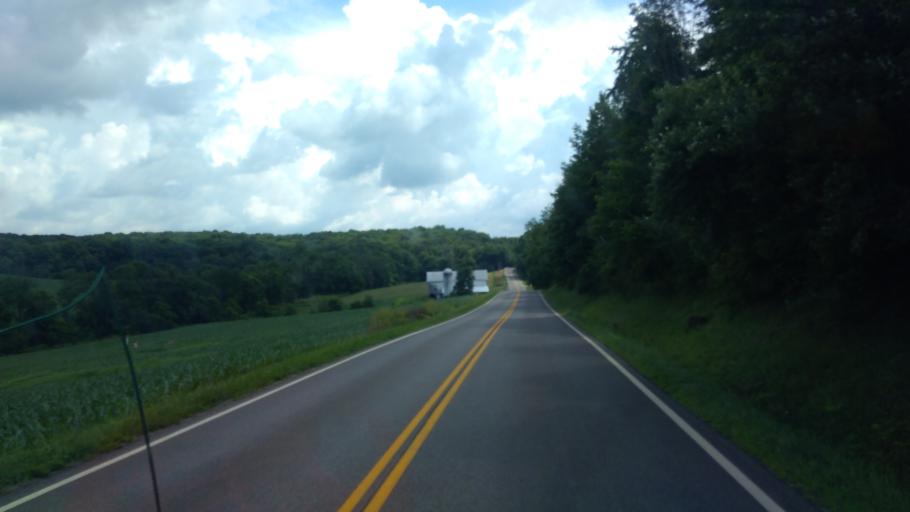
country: US
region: Ohio
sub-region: Ashland County
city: Loudonville
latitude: 40.7420
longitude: -82.2845
